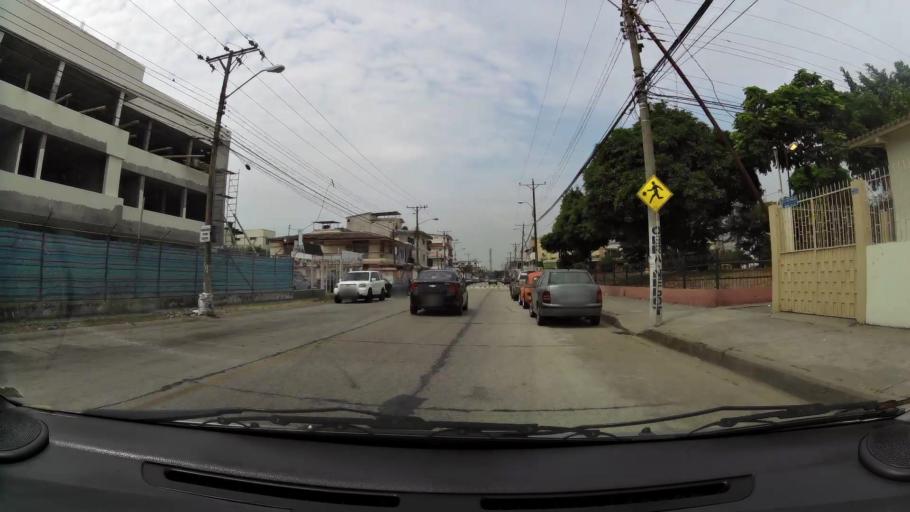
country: EC
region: Guayas
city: Eloy Alfaro
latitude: -2.1491
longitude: -79.8955
